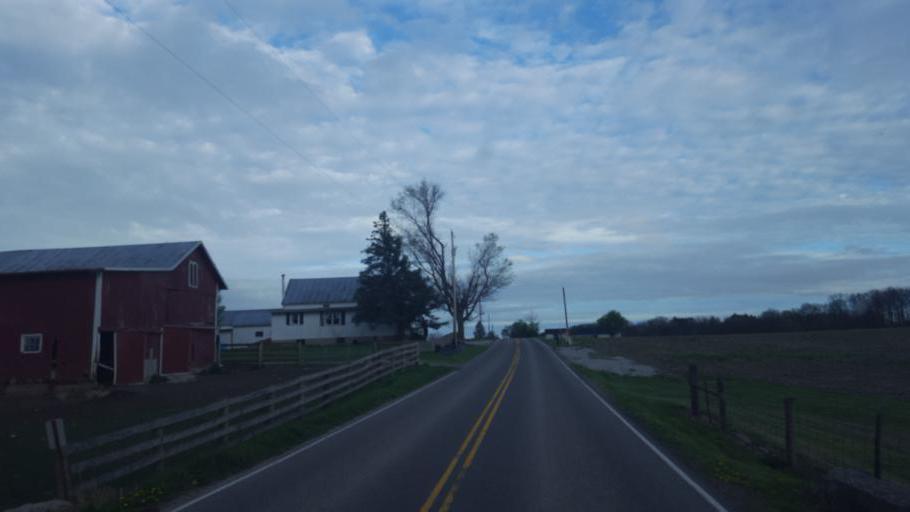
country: US
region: Ohio
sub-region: Knox County
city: Fredericktown
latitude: 40.5332
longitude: -82.6045
